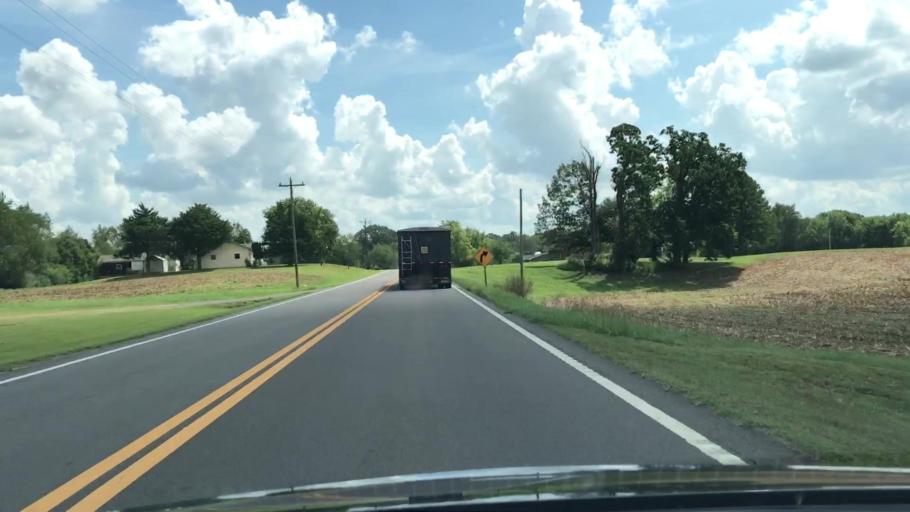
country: US
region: Tennessee
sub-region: Robertson County
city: Springfield
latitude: 36.6209
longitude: -86.9464
